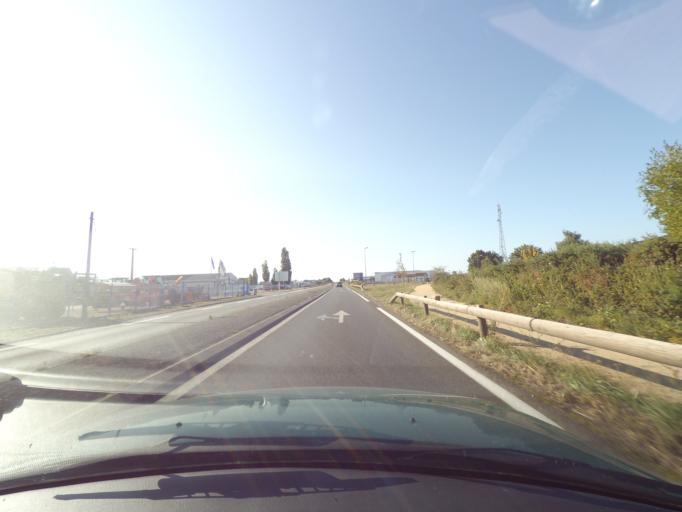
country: FR
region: Poitou-Charentes
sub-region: Departement des Deux-Sevres
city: Viennay
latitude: 46.6705
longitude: -0.2562
